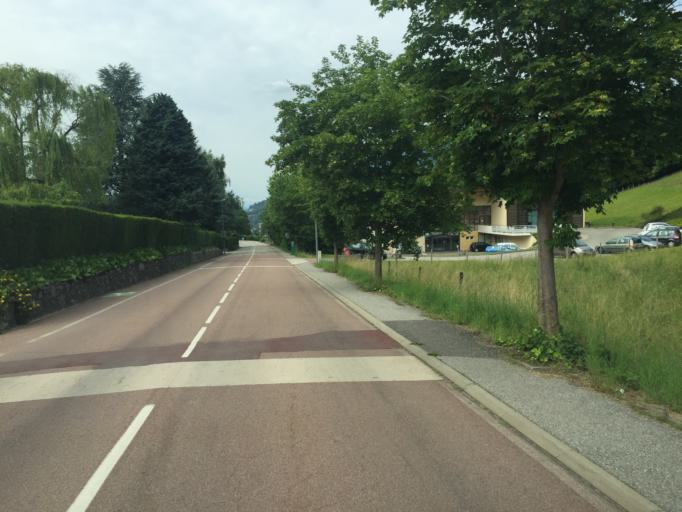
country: FR
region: Rhone-Alpes
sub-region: Departement de la Savoie
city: Jacob-Bellecombette
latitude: 45.5511
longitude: 5.9214
